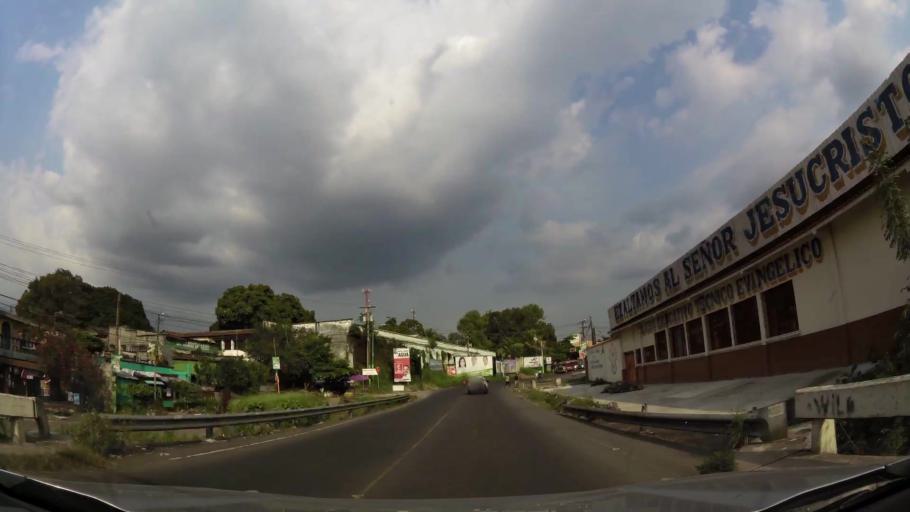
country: GT
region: Escuintla
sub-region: Municipio de Escuintla
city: Escuintla
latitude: 14.3053
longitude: -90.7894
